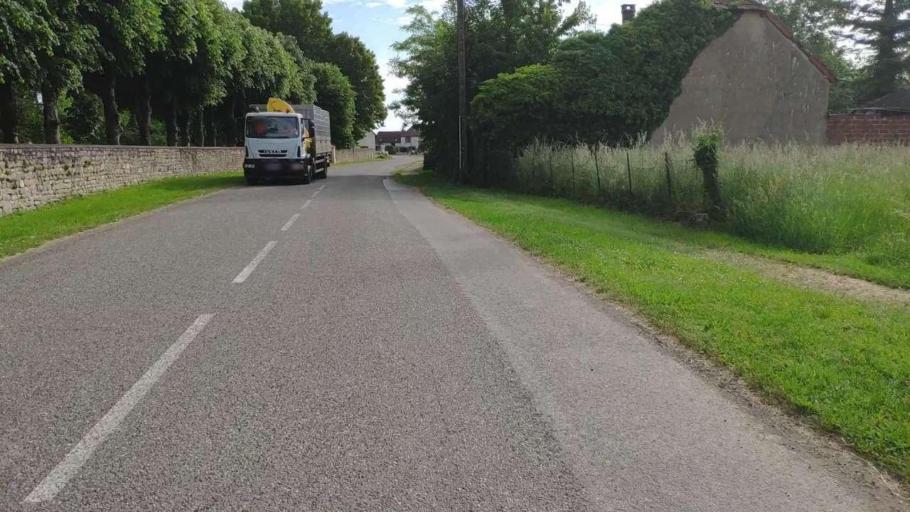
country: FR
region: Franche-Comte
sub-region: Departement du Jura
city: Bletterans
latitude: 46.7348
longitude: 5.4597
